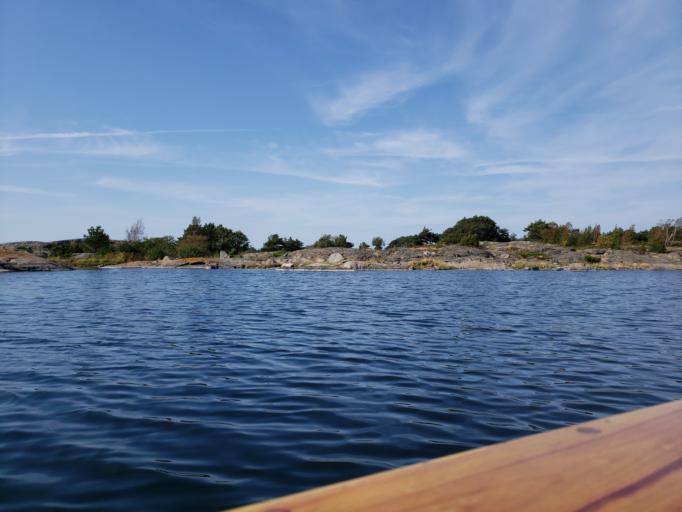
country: FI
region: Varsinais-Suomi
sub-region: Aboland-Turunmaa
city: Dragsfjaerd
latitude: 59.8474
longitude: 22.2072
